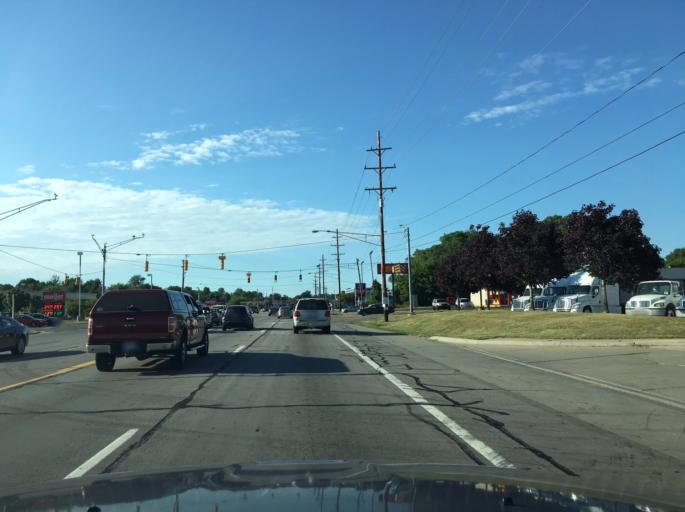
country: US
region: Michigan
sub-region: Macomb County
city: Clinton
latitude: 42.5947
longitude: -82.9003
